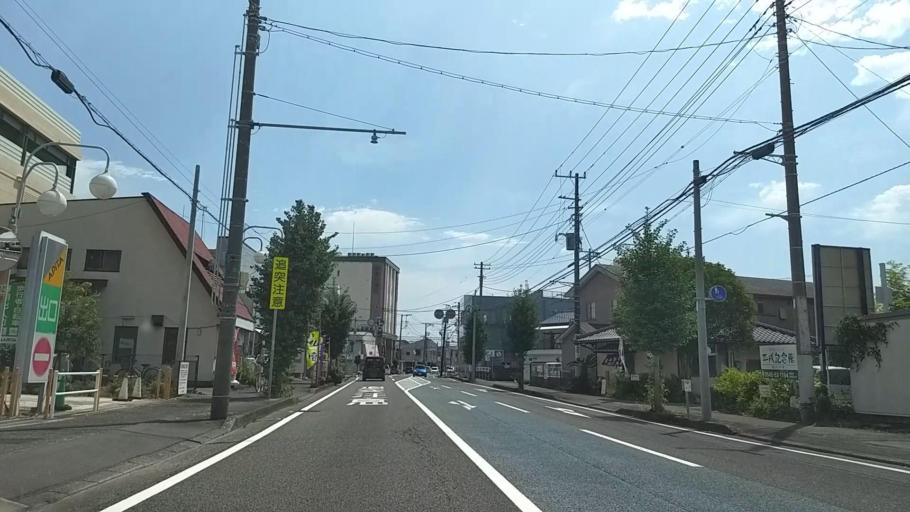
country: JP
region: Shizuoka
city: Fuji
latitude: 35.1681
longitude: 138.6801
